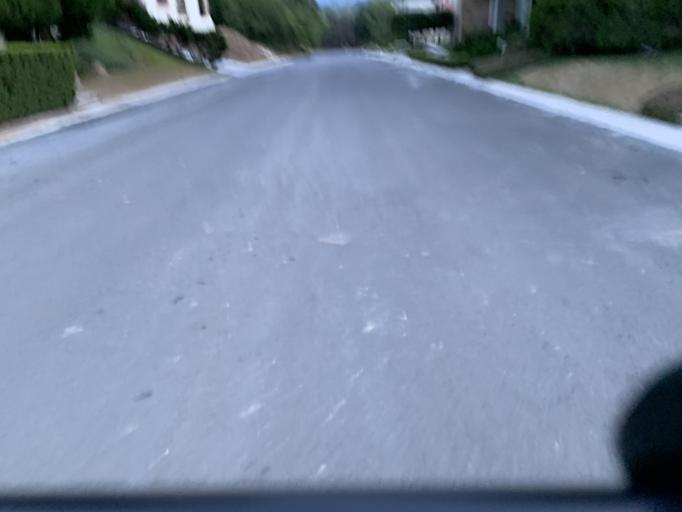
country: MX
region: Nuevo Leon
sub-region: Juarez
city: Bosques de San Pedro
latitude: 25.5204
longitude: -100.1892
